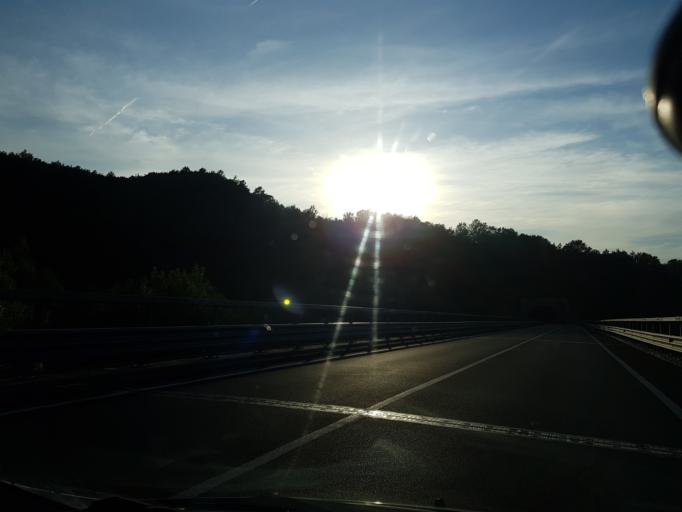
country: IT
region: Tuscany
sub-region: Provincia di Massa-Carrara
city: Fivizzano
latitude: 44.1998
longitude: 10.1045
